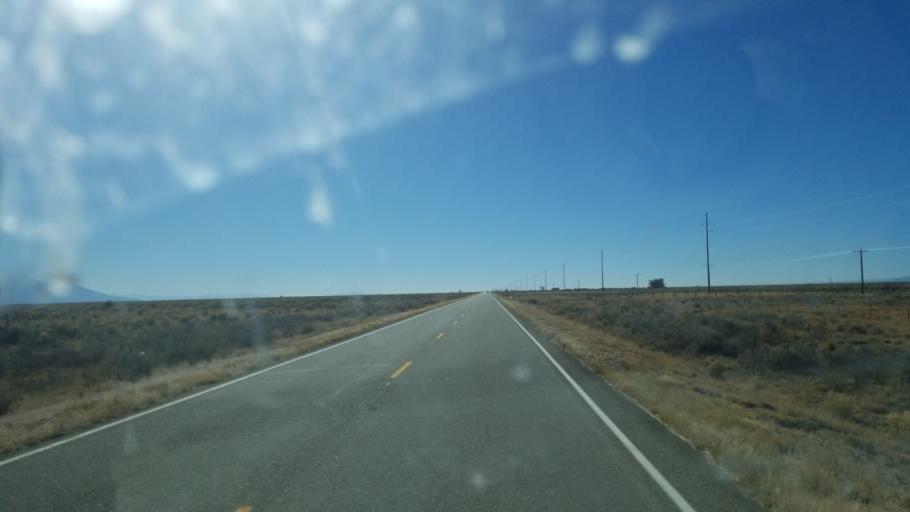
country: US
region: Colorado
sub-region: Saguache County
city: Saguache
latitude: 37.9868
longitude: -105.9072
